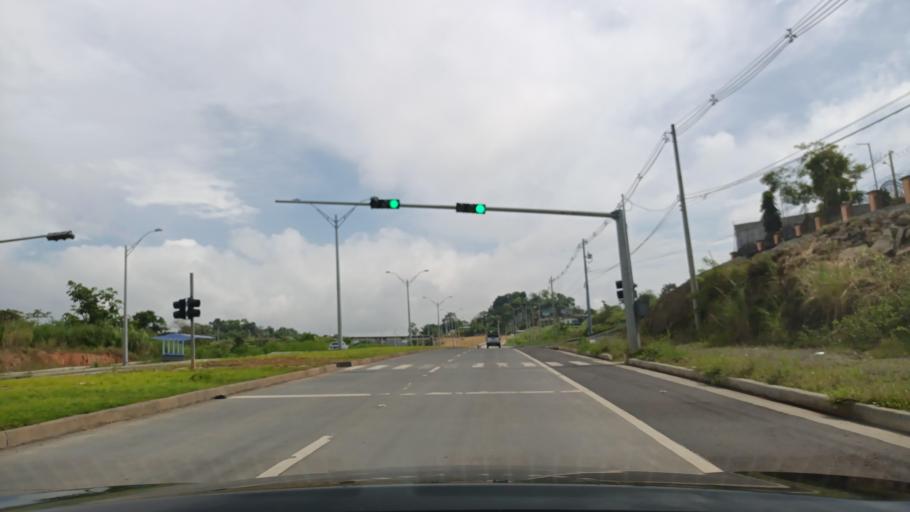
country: PA
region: Panama
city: Las Cumbres
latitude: 9.1001
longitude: -79.5022
